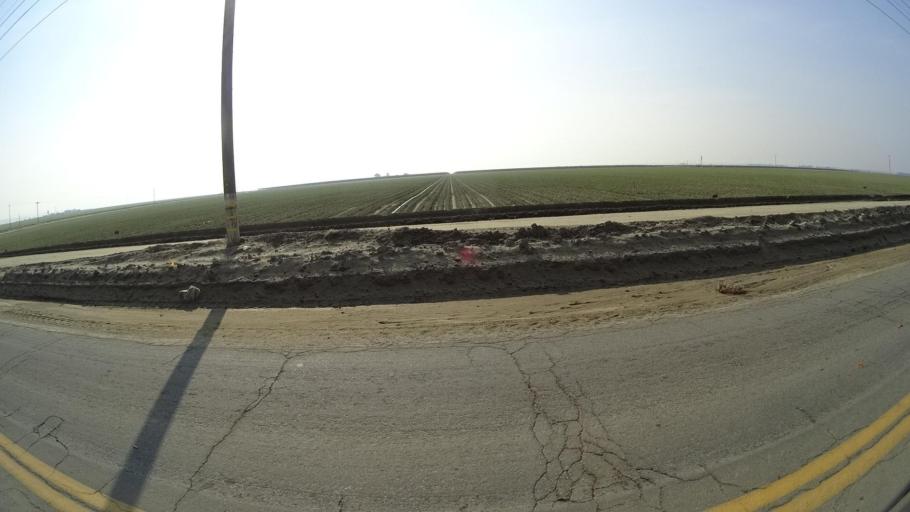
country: US
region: California
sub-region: Kern County
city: Arvin
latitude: 35.0928
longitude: -118.8486
